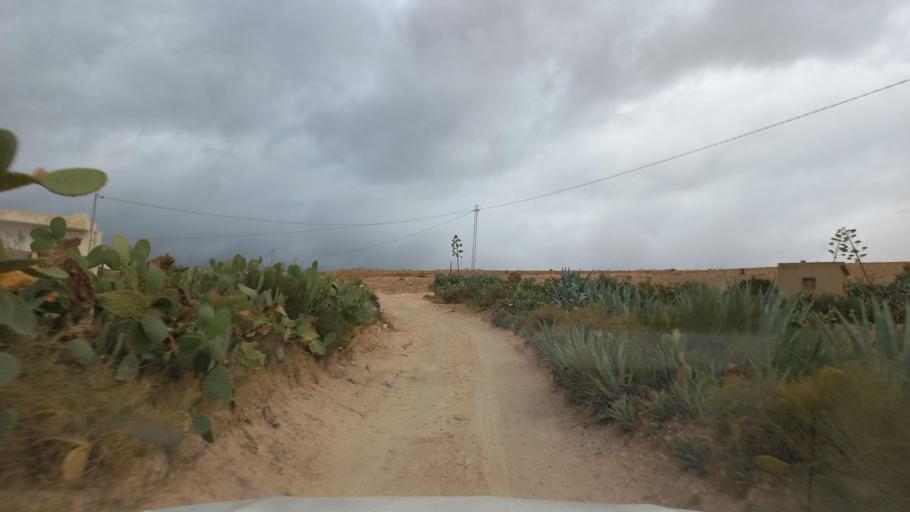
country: TN
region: Al Qasrayn
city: Kasserine
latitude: 35.2759
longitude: 8.9393
